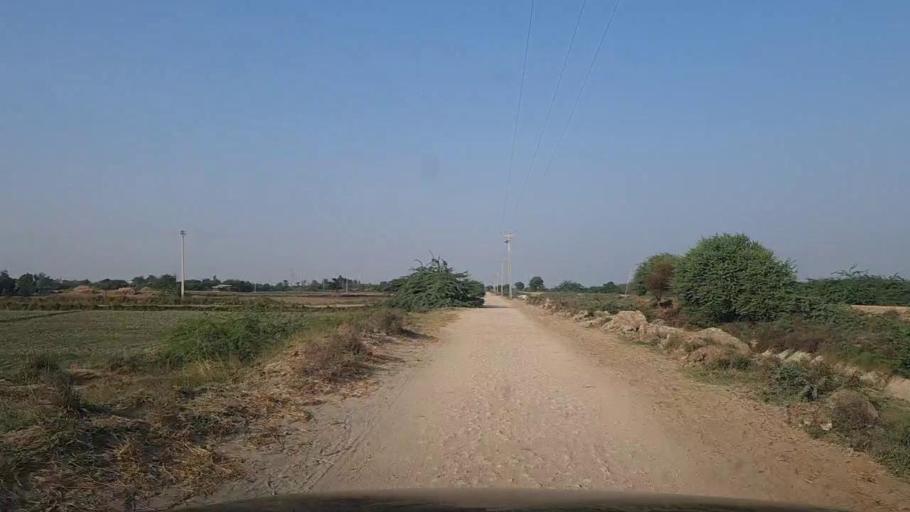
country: PK
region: Sindh
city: Thatta
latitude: 24.7499
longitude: 67.9585
